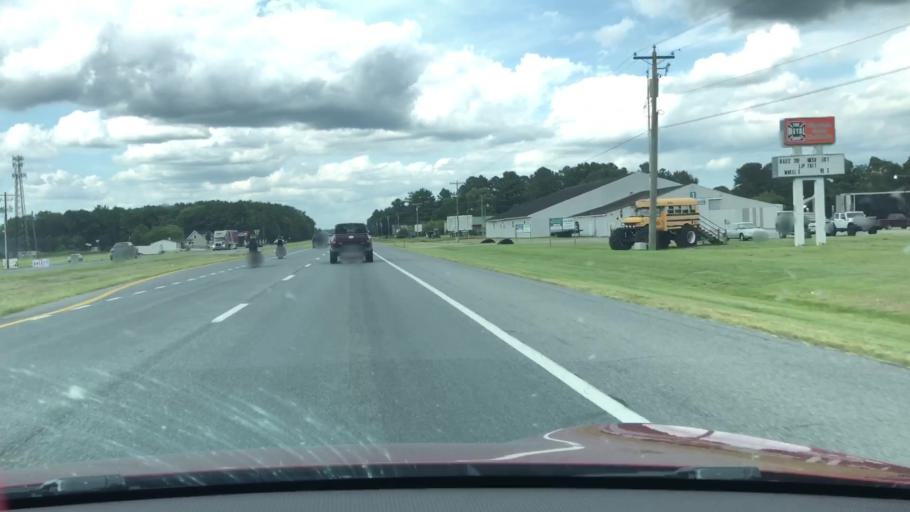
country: US
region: Delaware
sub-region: Sussex County
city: Delmar
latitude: 38.4651
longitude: -75.5579
